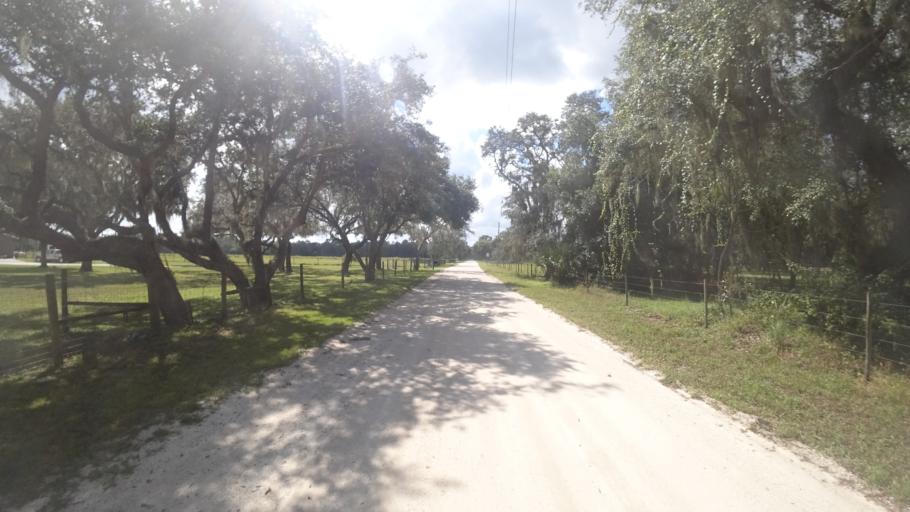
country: US
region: Florida
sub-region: Sarasota County
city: Lake Sarasota
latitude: 27.3862
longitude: -82.2190
